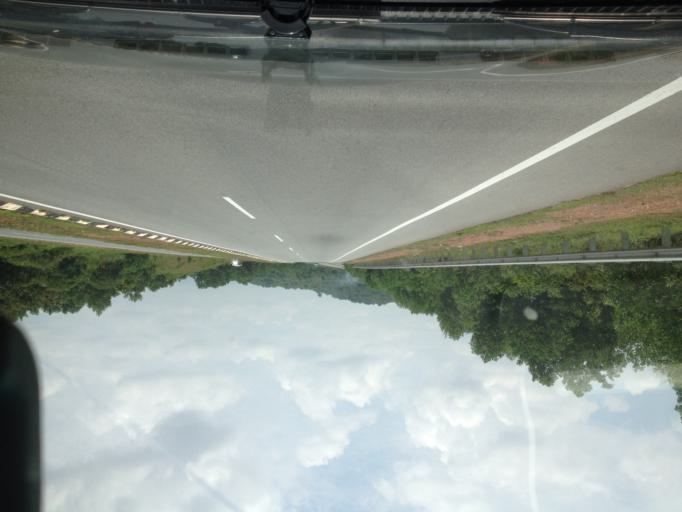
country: MY
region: Kedah
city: Sungai Petani
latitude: 5.6150
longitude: 100.5597
